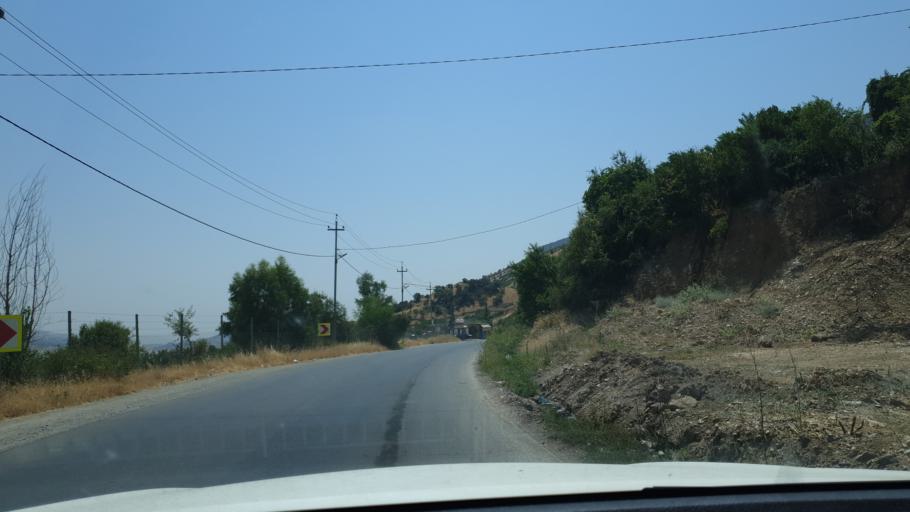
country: IQ
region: Arbil
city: Nahiyat Hiran
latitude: 36.2923
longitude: 44.4777
